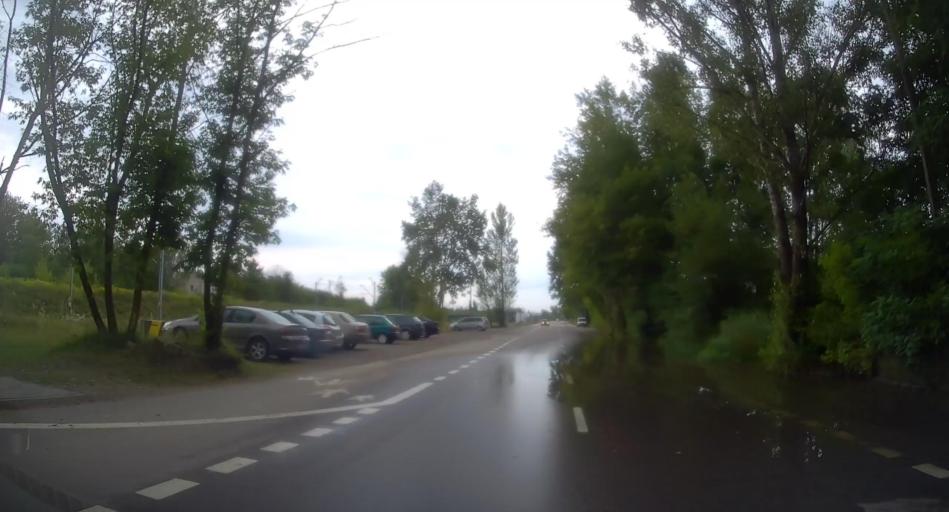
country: PL
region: Masovian Voivodeship
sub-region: Powiat piaseczynski
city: Piaseczno
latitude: 52.0681
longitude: 21.0165
